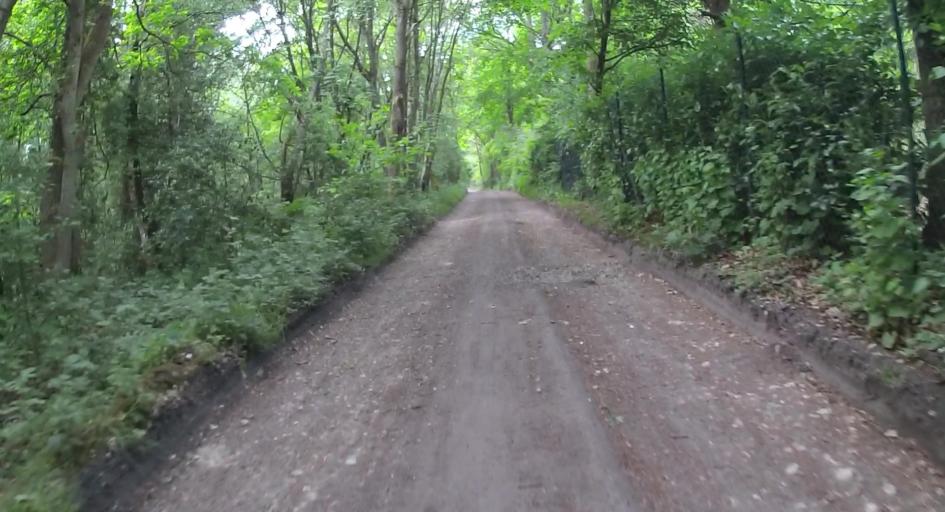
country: GB
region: England
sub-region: Surrey
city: Farnham
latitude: 51.2330
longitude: -0.8149
